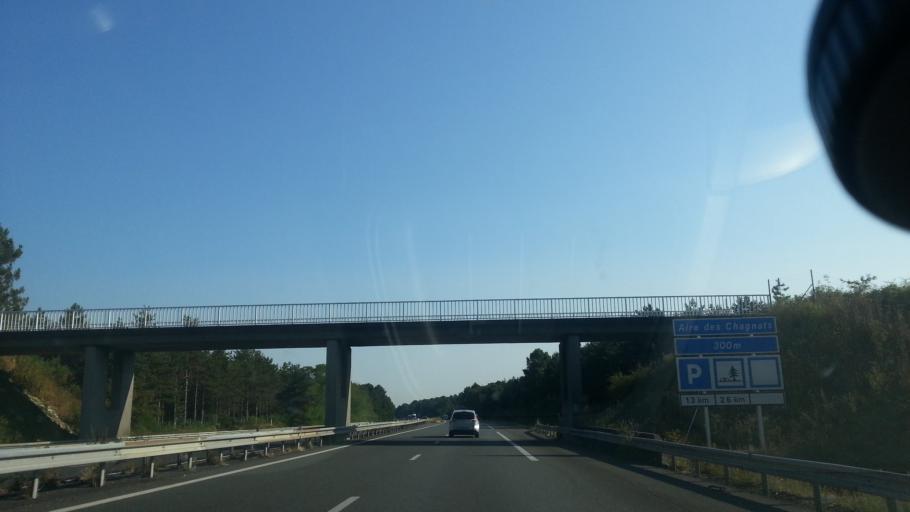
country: FR
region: Poitou-Charentes
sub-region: Departement de la Vienne
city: Chatellerault
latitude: 46.7878
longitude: 0.5067
